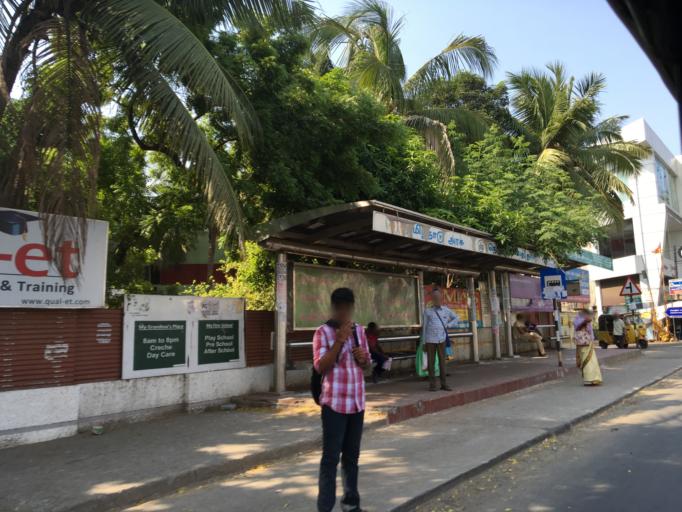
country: IN
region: Tamil Nadu
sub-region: Kancheepuram
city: Perungudi
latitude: 12.9816
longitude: 80.2304
